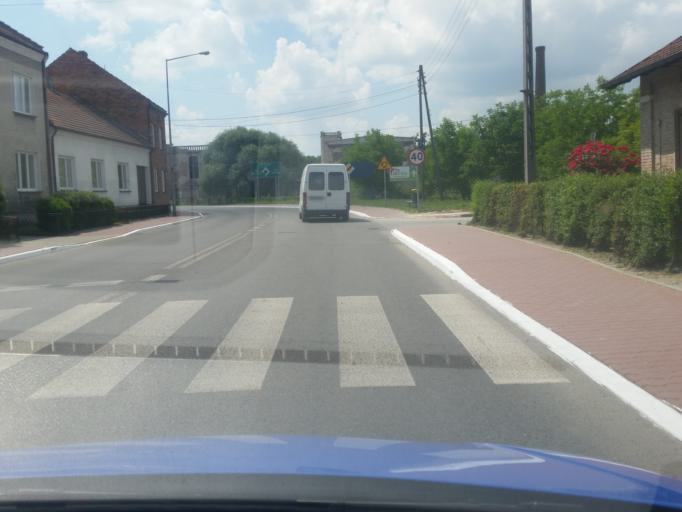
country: PL
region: Swietokrzyskie
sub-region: Powiat kazimierski
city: Kazimierza Wielka
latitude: 50.2667
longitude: 20.4957
